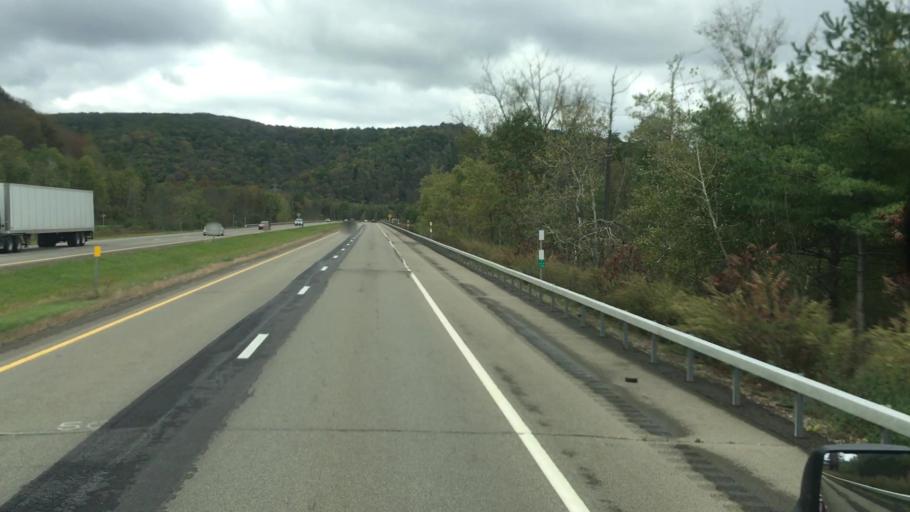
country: US
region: New York
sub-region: Cattaraugus County
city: Salamanca
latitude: 42.1030
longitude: -78.7992
